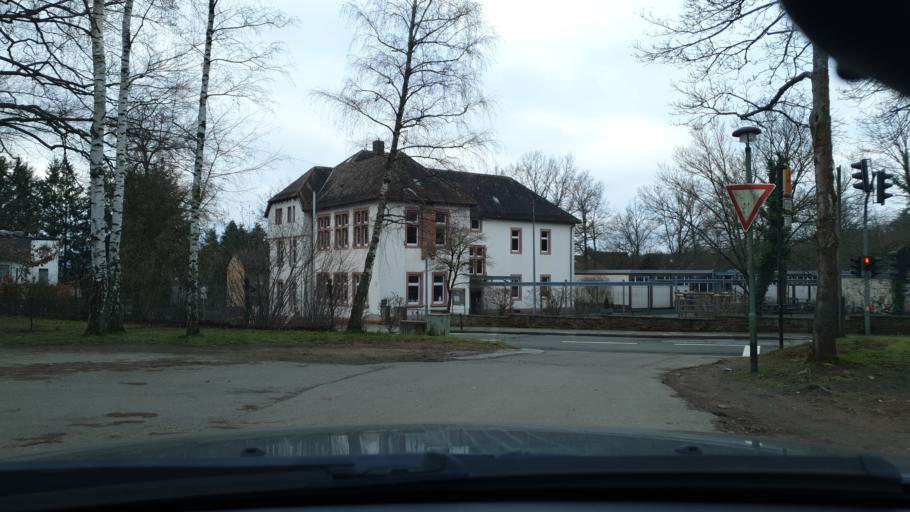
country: DE
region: Rheinland-Pfalz
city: Otterbach
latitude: 49.4597
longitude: 7.7313
